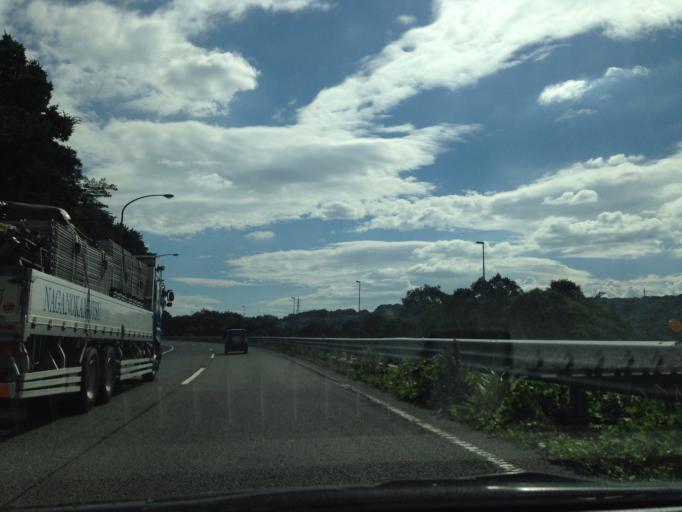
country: JP
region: Shizuoka
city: Gotemba
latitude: 35.3539
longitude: 138.9844
